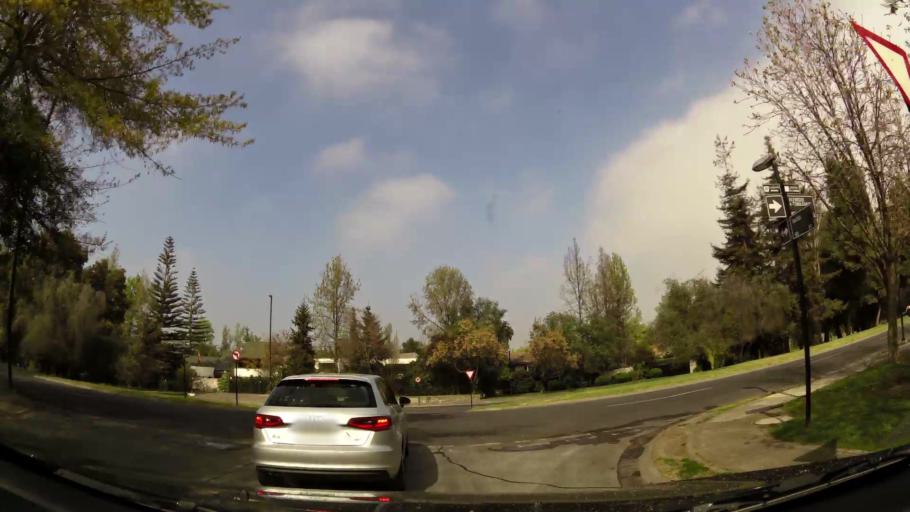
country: CL
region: Santiago Metropolitan
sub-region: Provincia de Santiago
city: Villa Presidente Frei, Nunoa, Santiago, Chile
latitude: -33.3706
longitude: -70.5730
